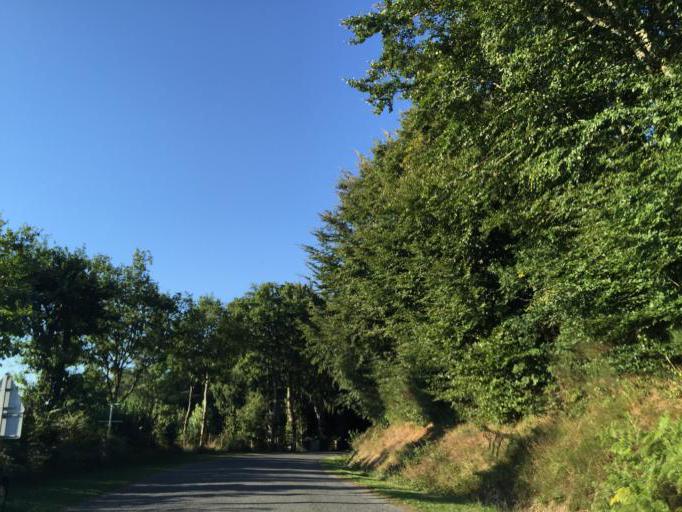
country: FR
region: Midi-Pyrenees
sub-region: Departement de l'Aveyron
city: Salles-Curan
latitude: 44.2022
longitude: 2.7774
